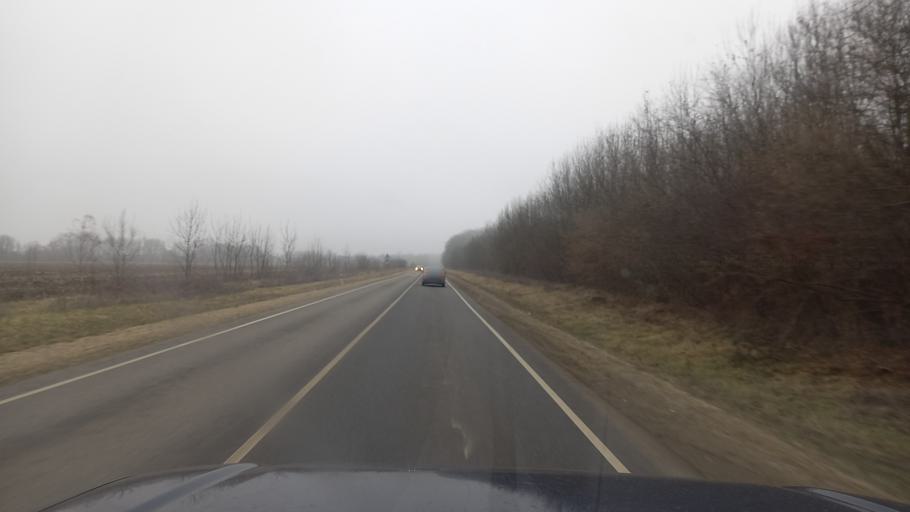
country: RU
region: Krasnodarskiy
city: Apsheronsk
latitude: 44.4250
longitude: 39.7840
